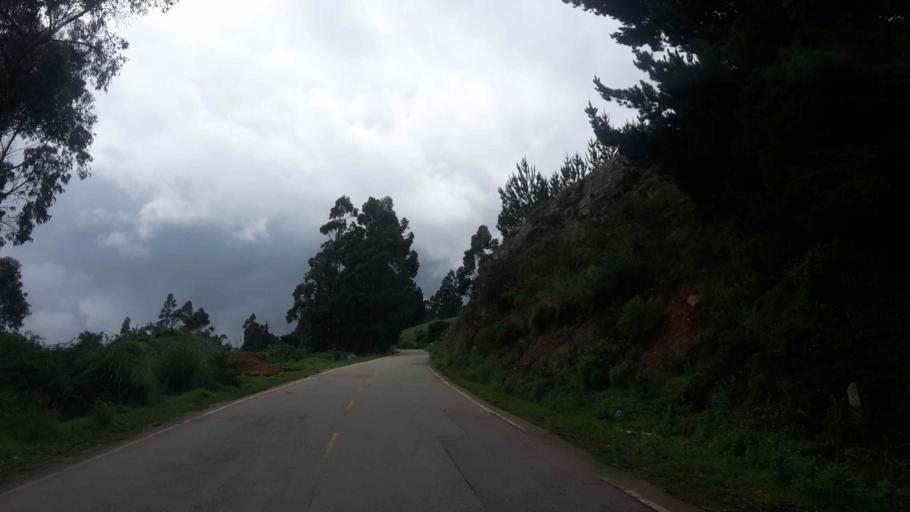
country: BO
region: Cochabamba
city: Totora
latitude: -17.5592
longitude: -65.3409
